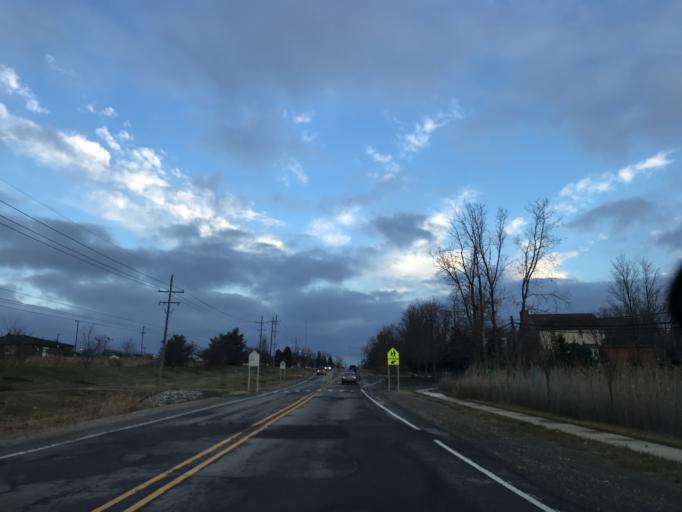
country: US
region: Michigan
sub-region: Oakland County
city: Novi
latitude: 42.4756
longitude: -83.4951
